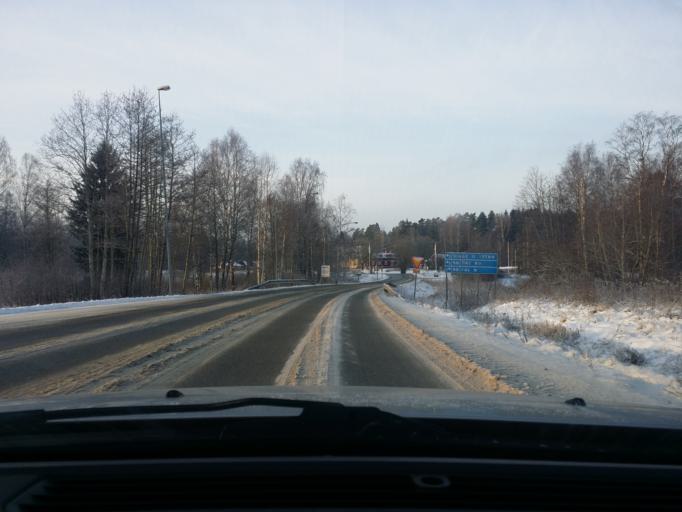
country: SE
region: OErebro
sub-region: Lindesbergs Kommun
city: Lindesberg
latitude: 59.6012
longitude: 15.1893
